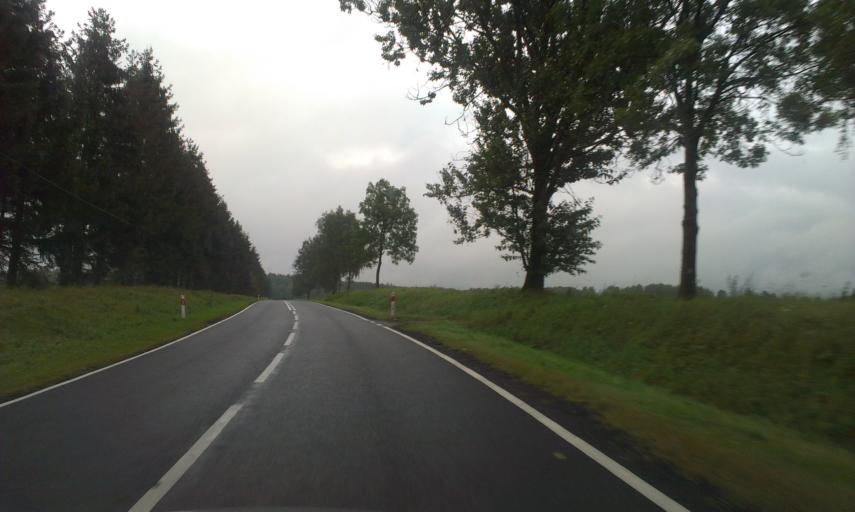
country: PL
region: West Pomeranian Voivodeship
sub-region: Powiat drawski
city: Czaplinek
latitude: 53.5733
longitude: 16.2676
